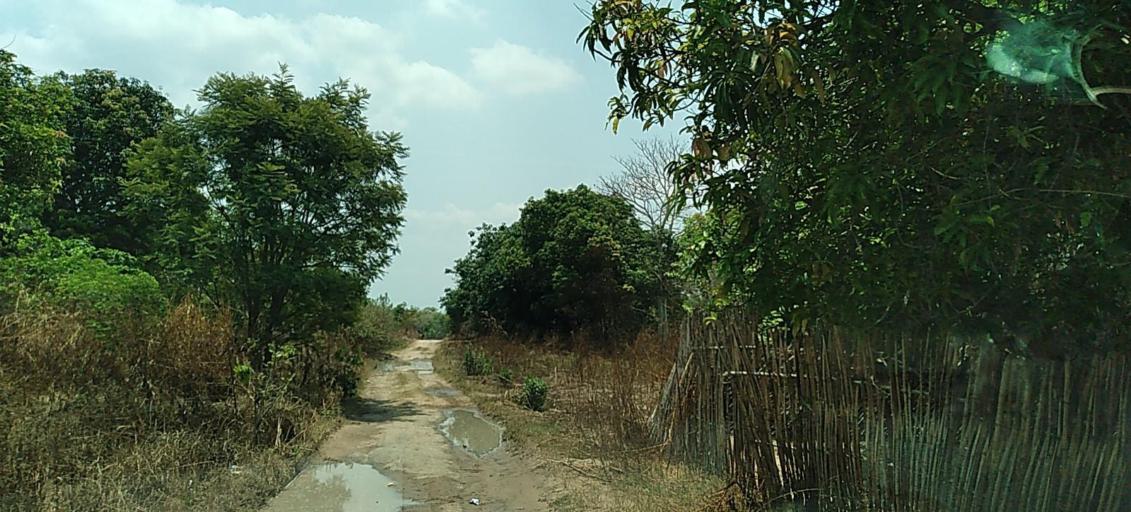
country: ZM
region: Copperbelt
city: Luanshya
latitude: -13.0956
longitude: 28.2885
